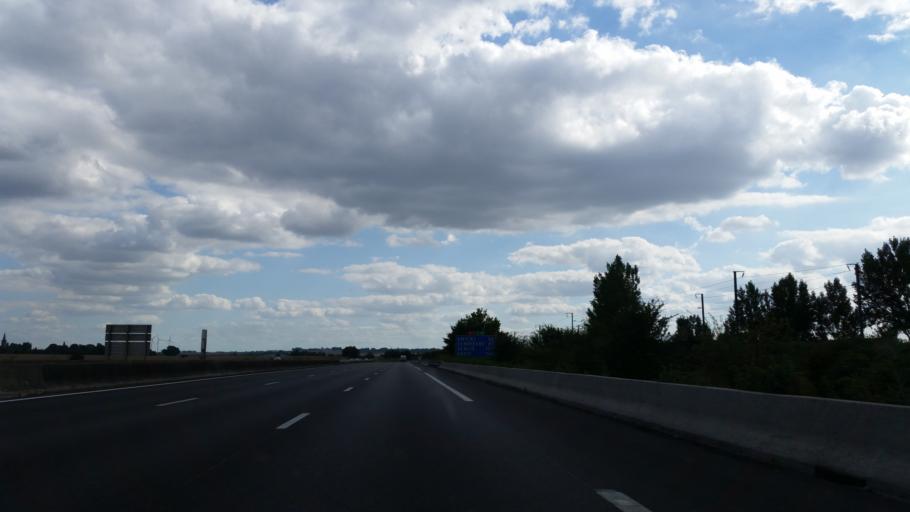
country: FR
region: Nord-Pas-de-Calais
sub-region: Departement du Pas-de-Calais
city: Bapaume
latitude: 50.0894
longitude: 2.8708
